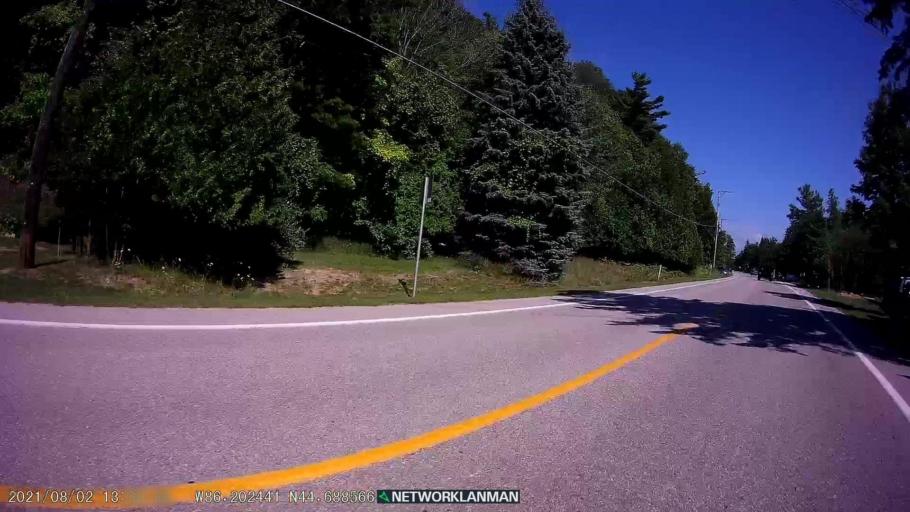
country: US
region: Michigan
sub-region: Benzie County
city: Frankfort
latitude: 44.6885
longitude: -86.2022
